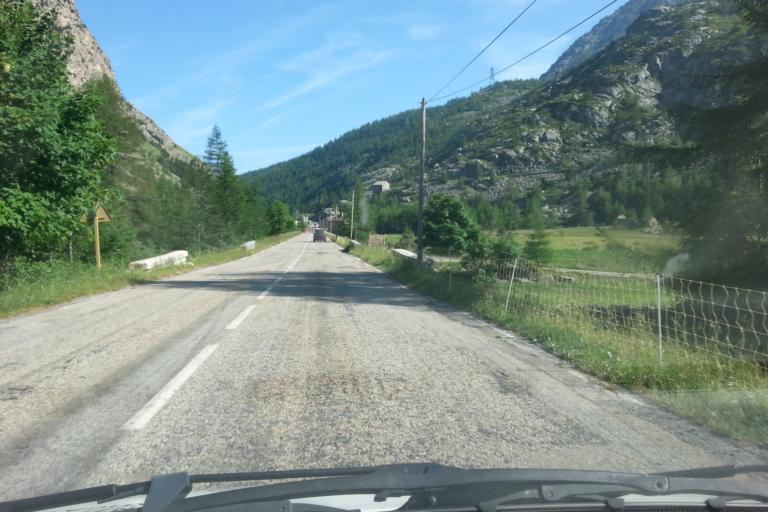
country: IT
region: Piedmont
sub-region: Provincia di Torino
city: Moncenisio
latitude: 45.2134
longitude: 6.9566
